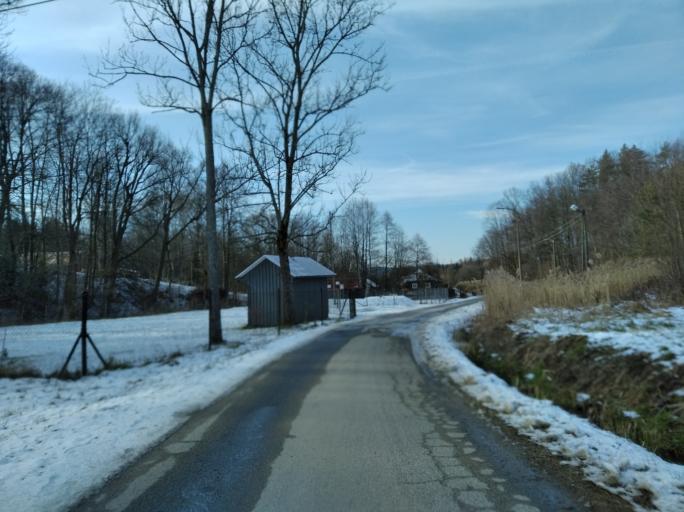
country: PL
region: Subcarpathian Voivodeship
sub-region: Powiat krosnienski
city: Korczyna
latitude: 49.7679
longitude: 21.7998
